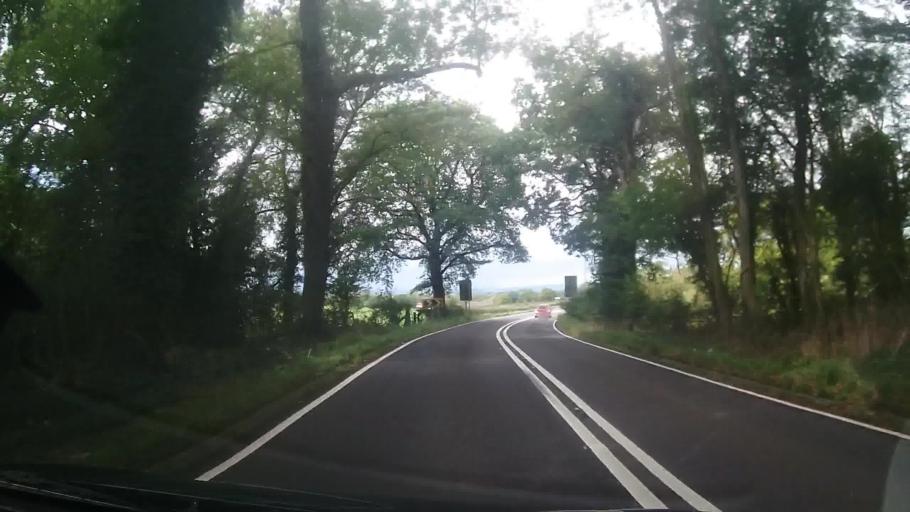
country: GB
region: England
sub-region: Shropshire
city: Romsley
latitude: 52.4394
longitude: -2.3286
